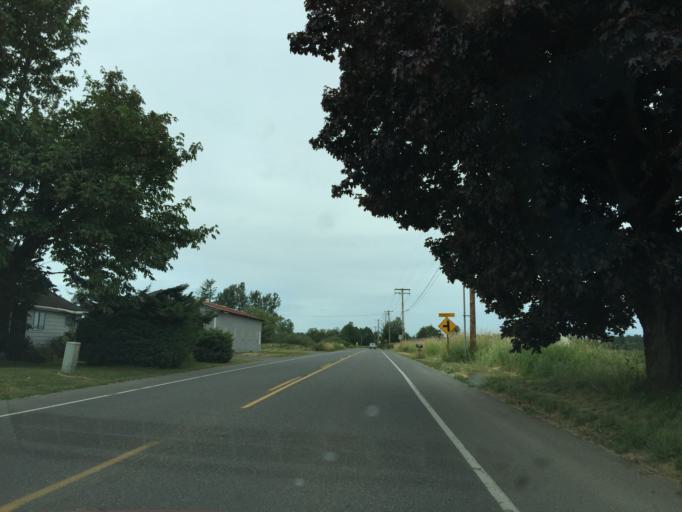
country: US
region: Washington
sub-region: Whatcom County
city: Everson
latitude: 48.9402
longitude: -122.3423
